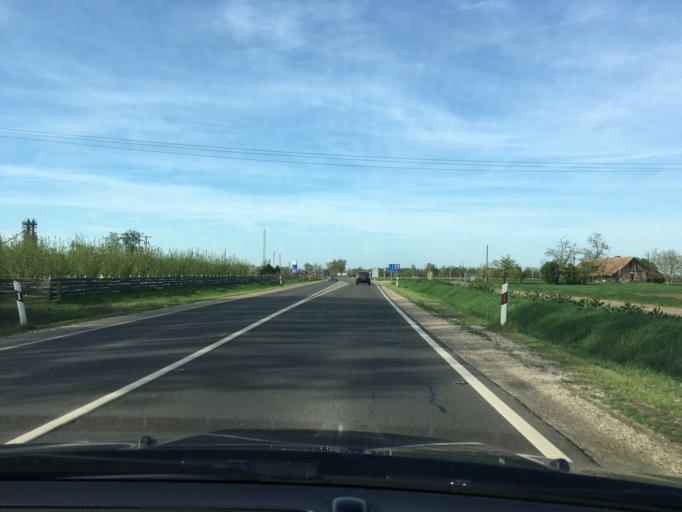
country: HU
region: Bekes
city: Mezobereny
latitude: 46.8026
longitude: 21.0059
